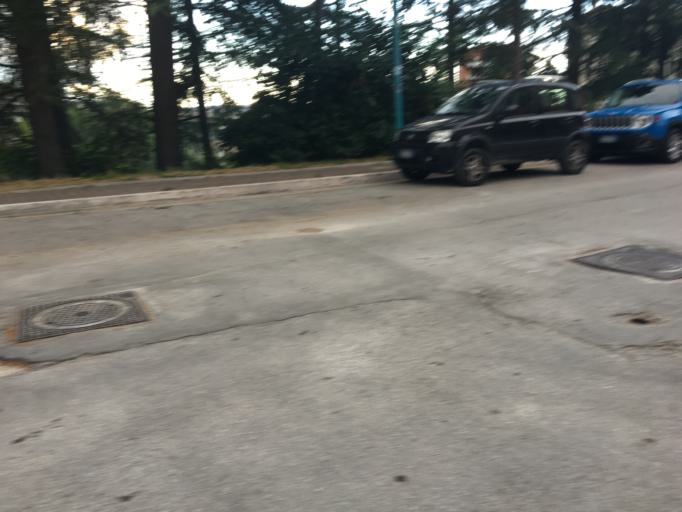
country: IT
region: Molise
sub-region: Provincia di Campobasso
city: Campobasso
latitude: 41.5571
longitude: 14.6546
